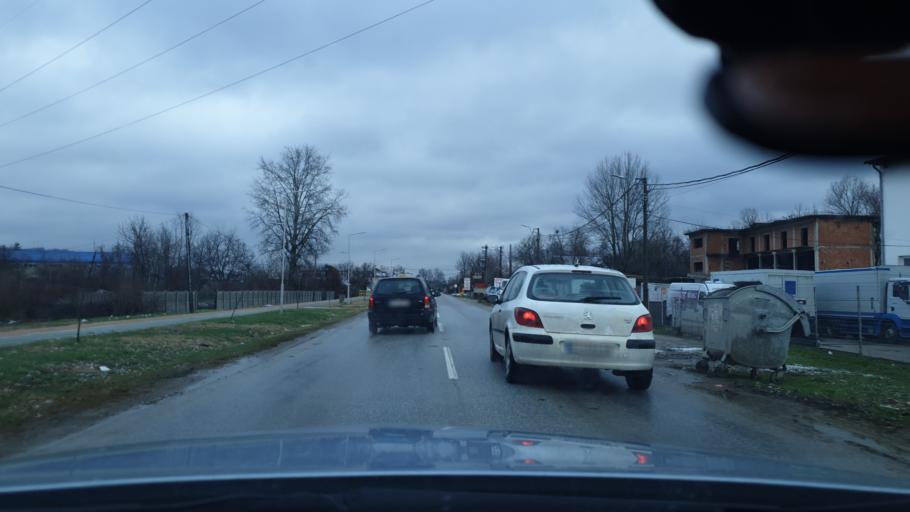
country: RS
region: Central Serbia
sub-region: Branicevski Okrug
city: Petrovac
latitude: 44.3941
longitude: 21.4054
